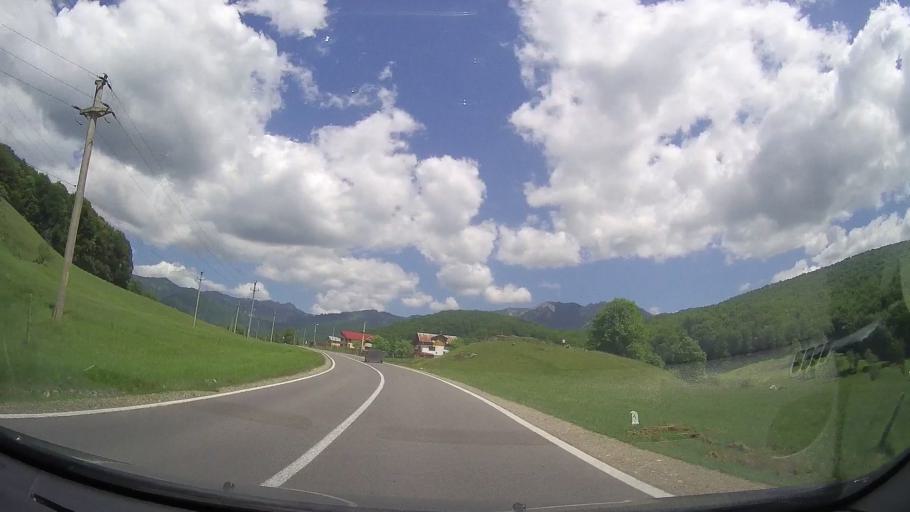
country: RO
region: Prahova
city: Maneciu
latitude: 45.4395
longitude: 25.9389
